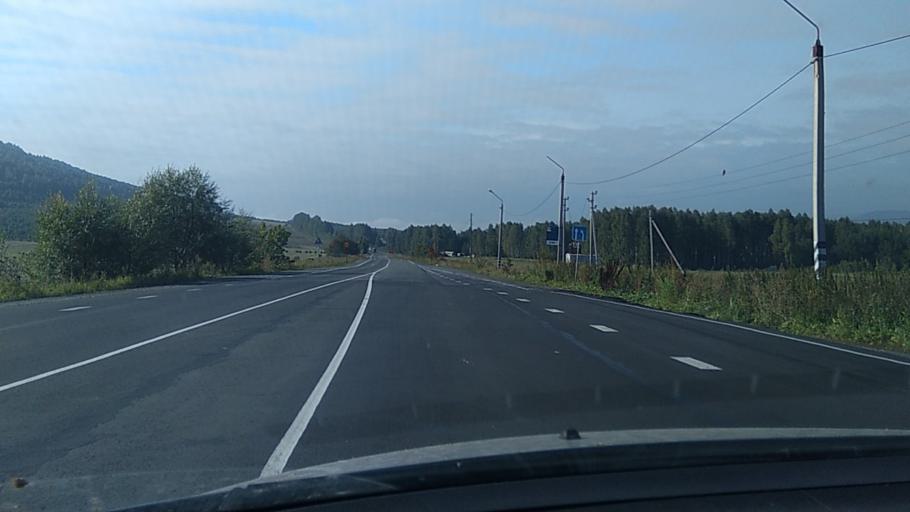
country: RU
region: Chelyabinsk
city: Karabash
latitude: 55.3822
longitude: 60.2559
